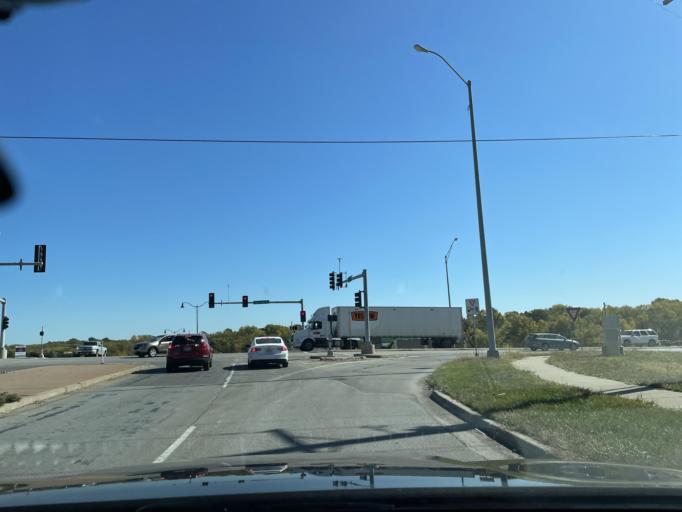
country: US
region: Missouri
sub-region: Andrew County
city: Country Club Village
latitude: 39.8123
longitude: -94.8070
